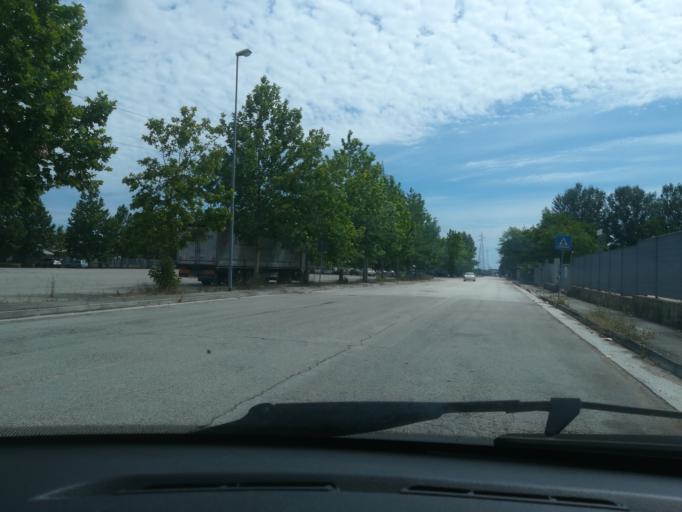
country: IT
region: The Marches
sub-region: Provincia di Macerata
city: Santa Maria Apparente
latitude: 43.2834
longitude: 13.6761
